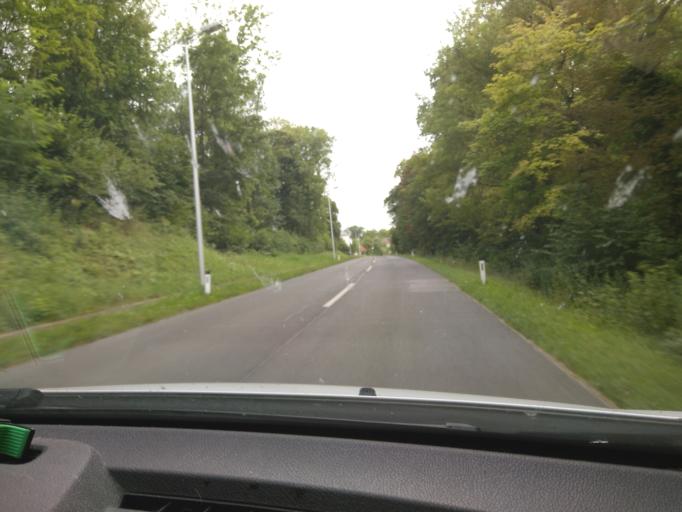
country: AT
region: Burgenland
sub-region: Politischer Bezirk Oberpullendorf
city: Nikitsch
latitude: 47.5320
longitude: 16.6494
